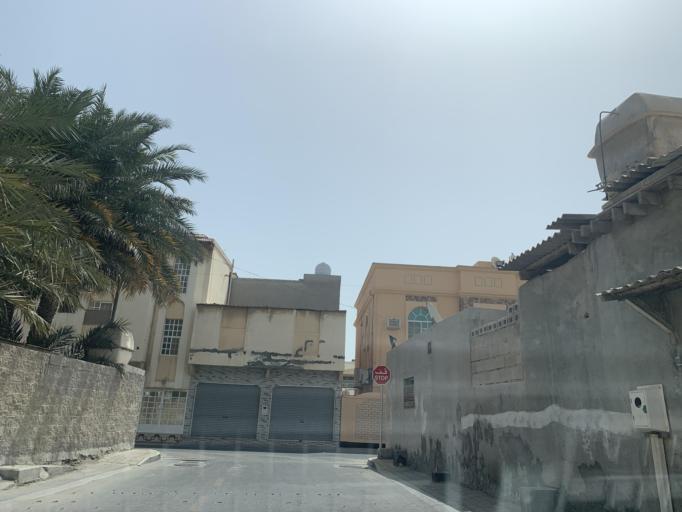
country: BH
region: Northern
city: Sitrah
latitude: 26.1361
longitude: 50.5996
